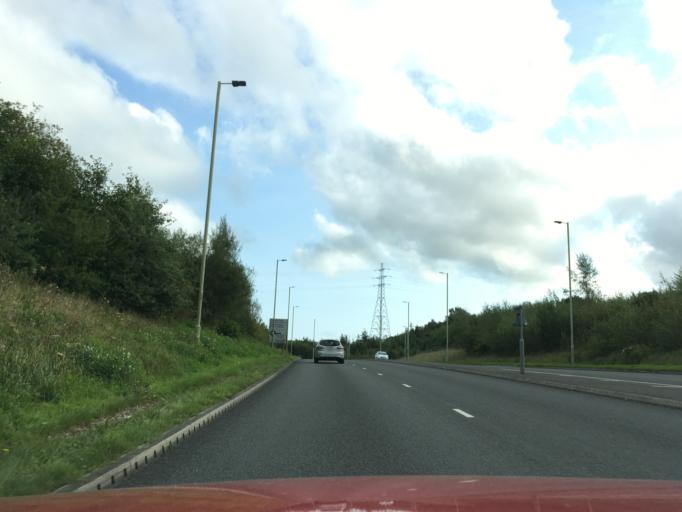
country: GB
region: Wales
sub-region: Rhondda Cynon Taf
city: Llantwit Fardre
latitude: 51.5720
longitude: -3.3046
